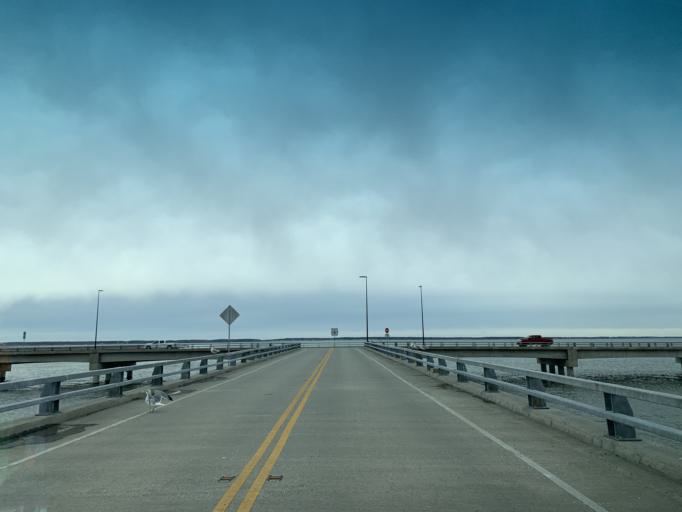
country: US
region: Virginia
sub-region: Accomack County
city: Chincoteague
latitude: 37.9370
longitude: -75.3811
